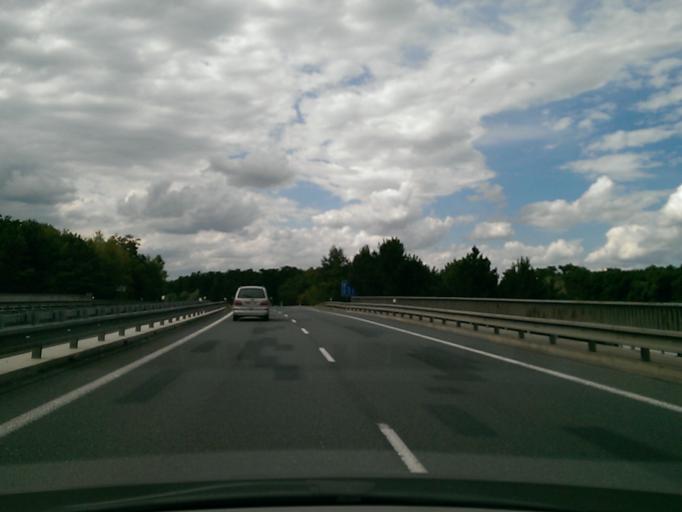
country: CZ
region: Central Bohemia
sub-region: Okres Nymburk
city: Podebrady
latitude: 50.1177
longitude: 15.1252
